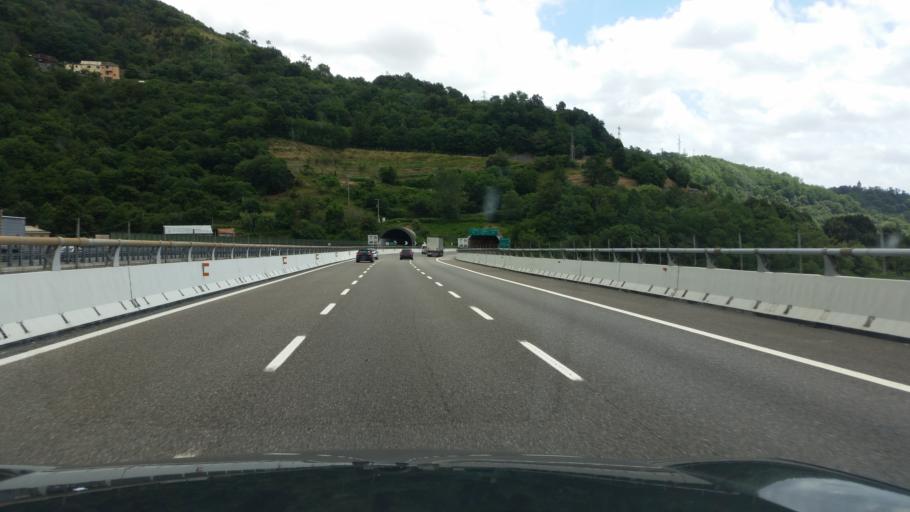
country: IT
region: Liguria
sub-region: Provincia di Genova
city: Mele
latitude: 44.4427
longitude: 8.7295
